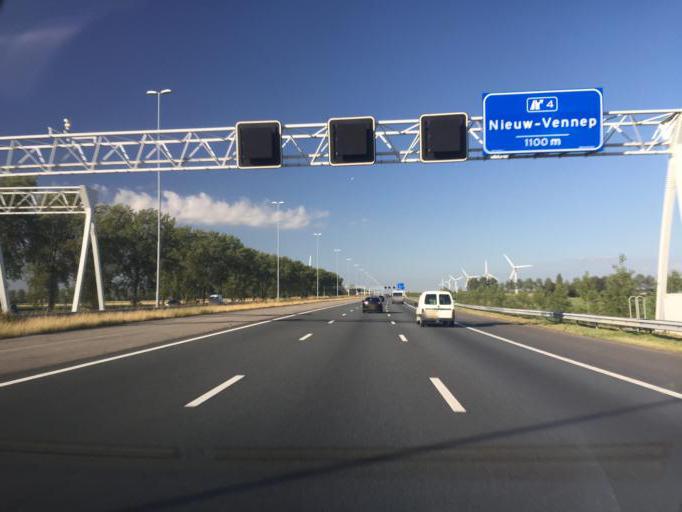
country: NL
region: South Holland
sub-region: Gemeente Kaag en Braassem
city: Oude Wetering
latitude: 52.2219
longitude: 4.6323
